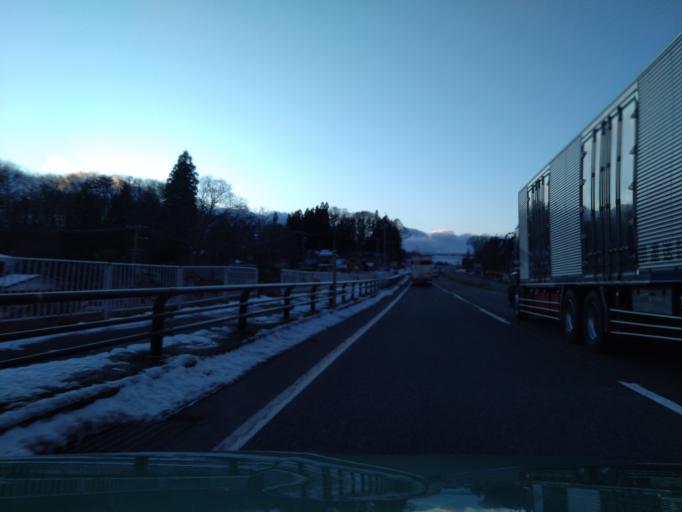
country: JP
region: Iwate
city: Shizukuishi
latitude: 39.7019
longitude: 141.0441
